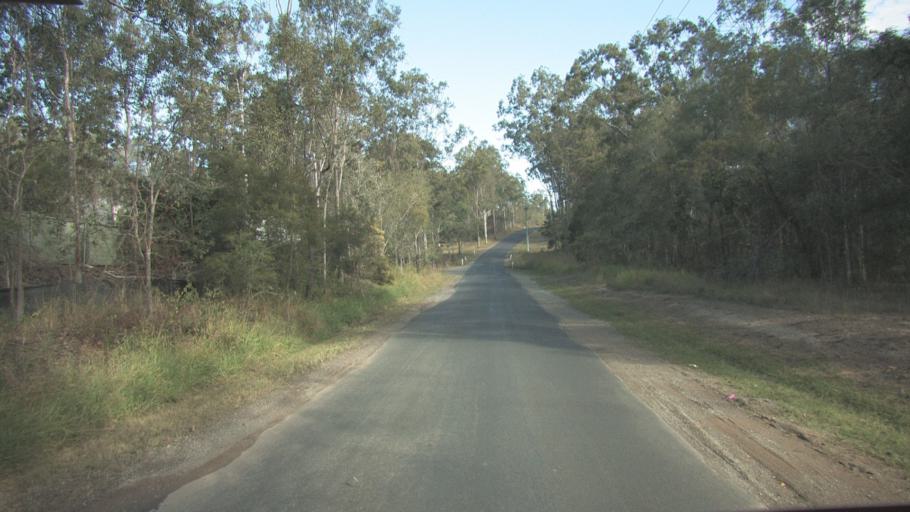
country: AU
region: Queensland
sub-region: Logan
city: Cedar Vale
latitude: -27.8313
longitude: 153.0615
